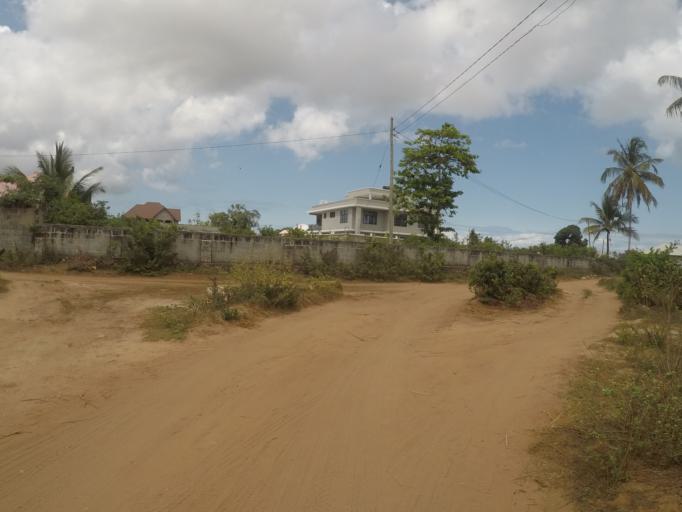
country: TZ
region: Zanzibar Urban/West
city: Zanzibar
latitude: -6.2028
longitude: 39.2320
